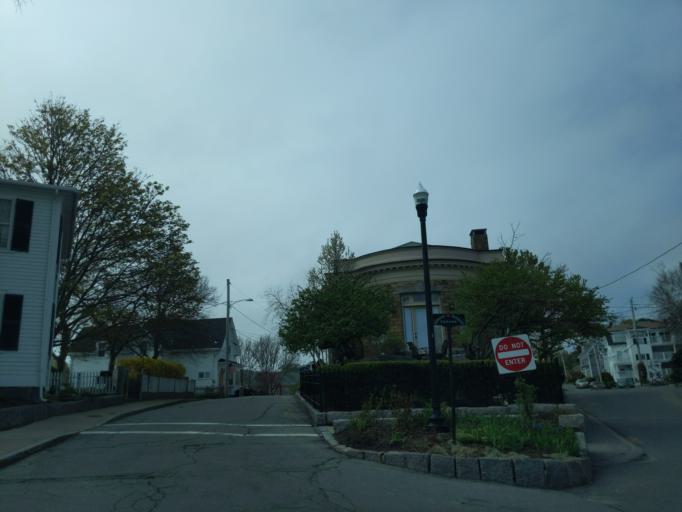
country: US
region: Massachusetts
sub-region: Essex County
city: Rockport
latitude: 42.6581
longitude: -70.6193
